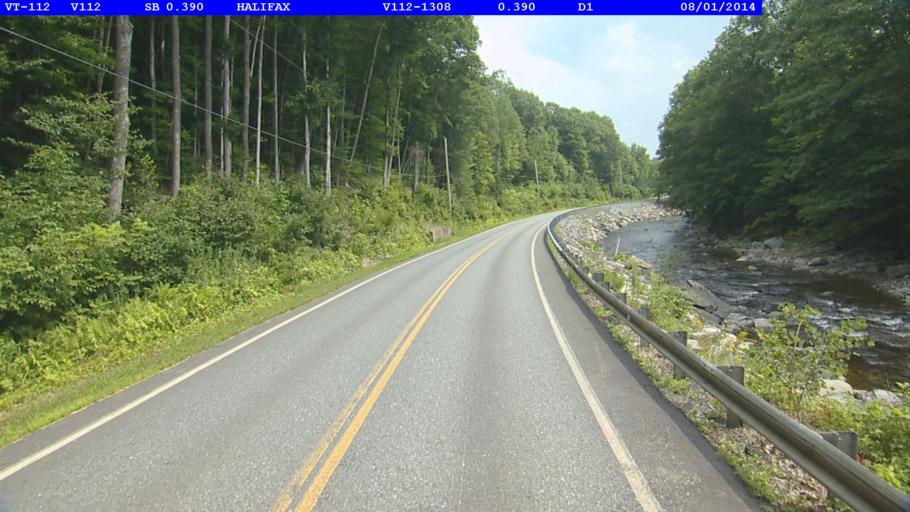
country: US
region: Massachusetts
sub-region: Franklin County
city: Colrain
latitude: 42.7389
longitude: -72.7259
